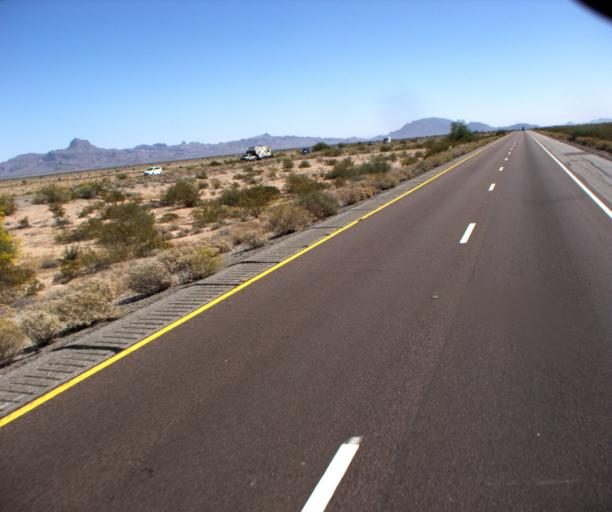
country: US
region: Arizona
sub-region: La Paz County
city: Salome
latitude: 33.5552
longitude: -113.2639
